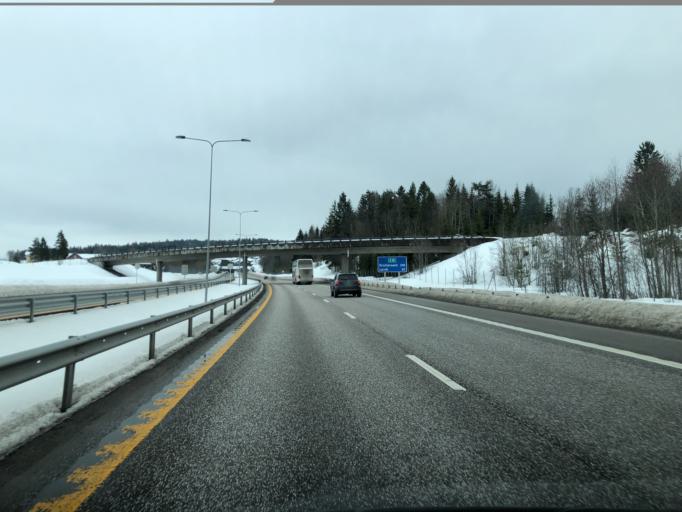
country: NO
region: Vestfold
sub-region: Holmestrand
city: Gullhaug
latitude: 59.5033
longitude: 10.2155
